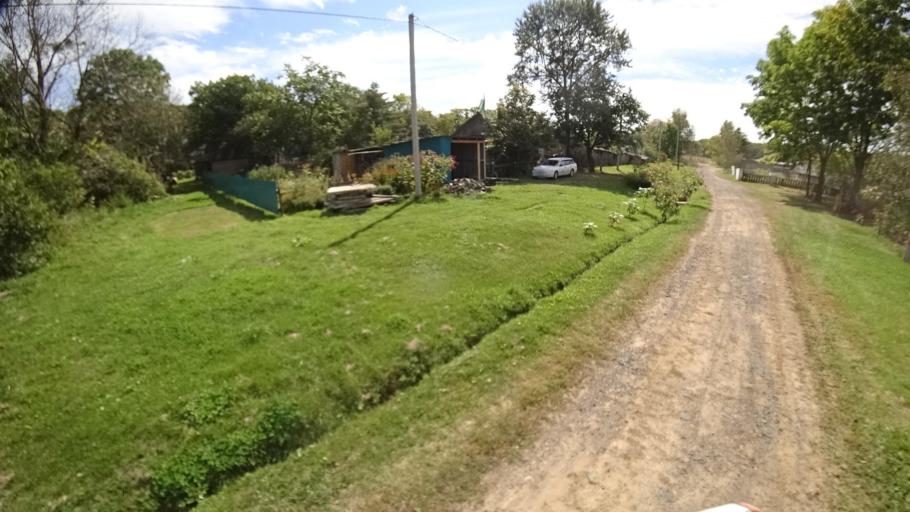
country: RU
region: Primorskiy
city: Yakovlevka
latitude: 44.7073
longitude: 133.6421
